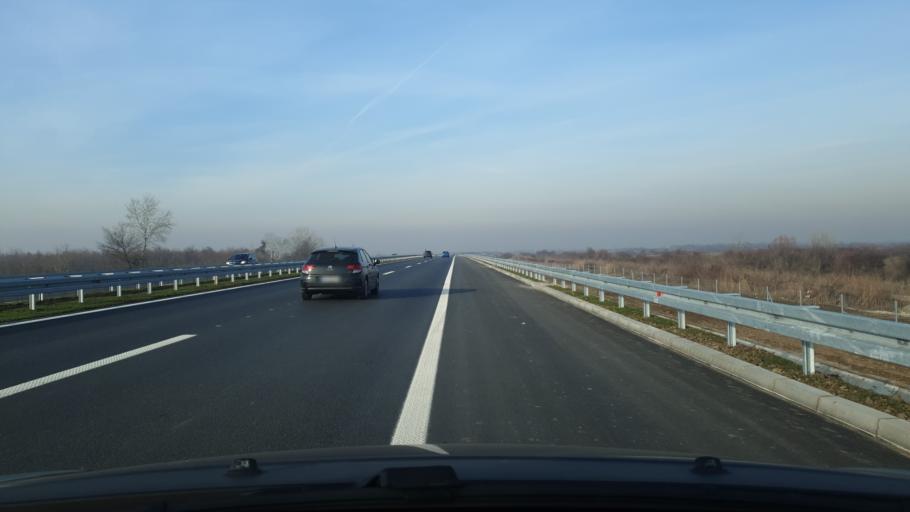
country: RS
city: Boljevci
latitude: 44.7023
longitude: 20.2634
